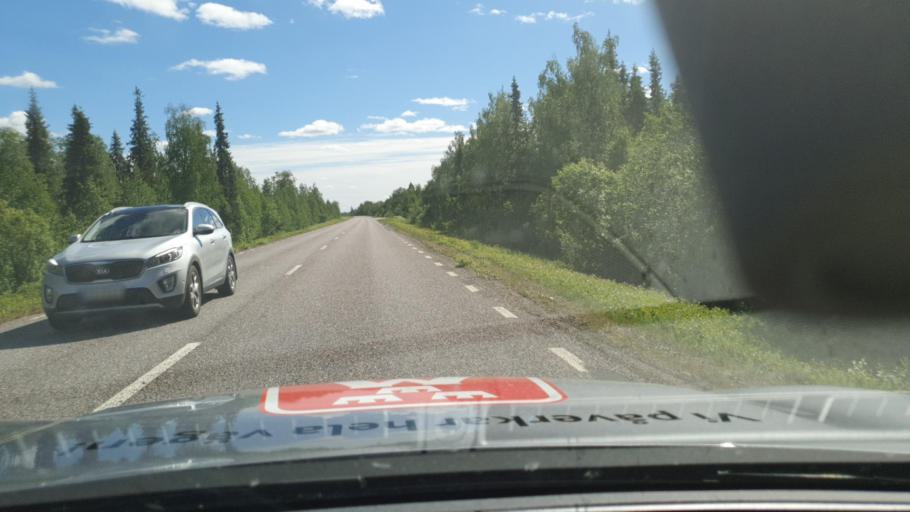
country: SE
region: Norrbotten
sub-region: Pajala Kommun
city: Pajala
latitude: 67.1303
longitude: 23.5894
